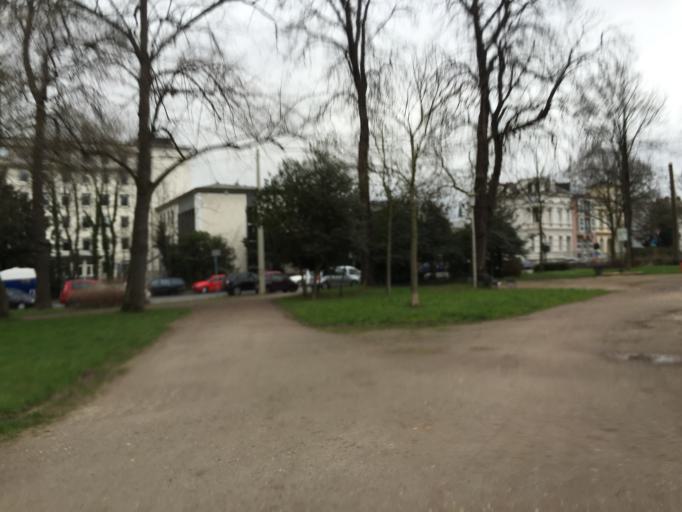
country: DE
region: North Rhine-Westphalia
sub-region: Regierungsbezirk Koln
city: Bonn
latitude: 50.7312
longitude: 7.0889
